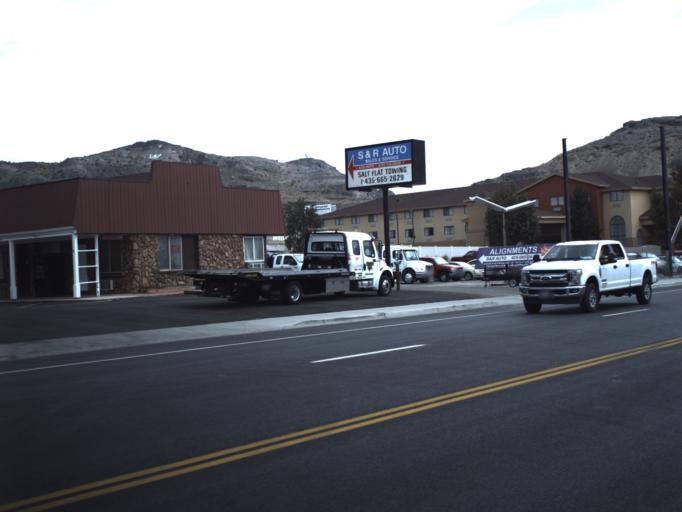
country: US
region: Utah
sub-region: Tooele County
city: Wendover
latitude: 40.7376
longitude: -114.0352
